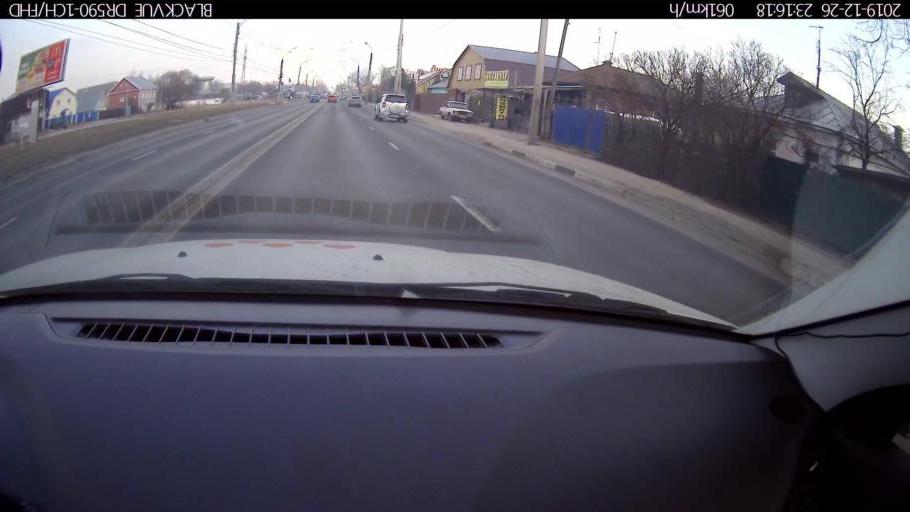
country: RU
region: Nizjnij Novgorod
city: Burevestnik
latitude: 56.2208
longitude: 43.8479
